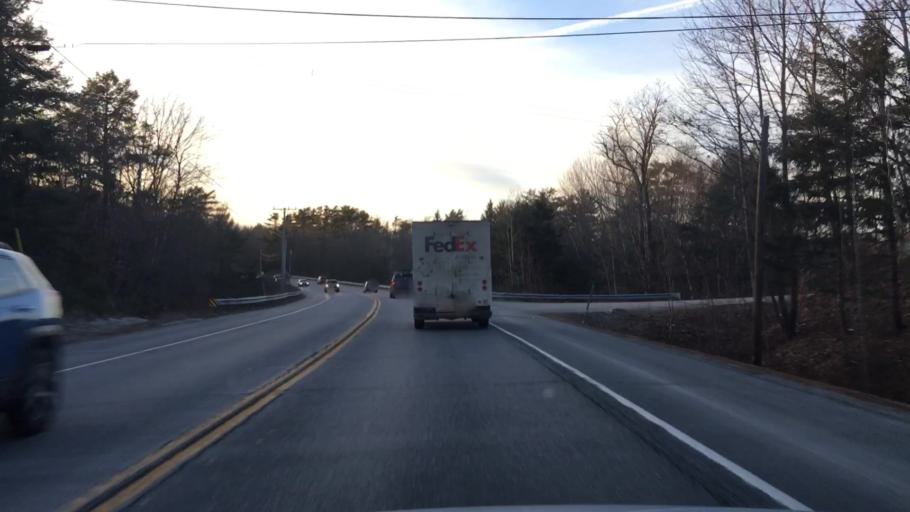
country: US
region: Maine
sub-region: Penobscot County
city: Holden
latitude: 44.7556
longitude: -68.6638
